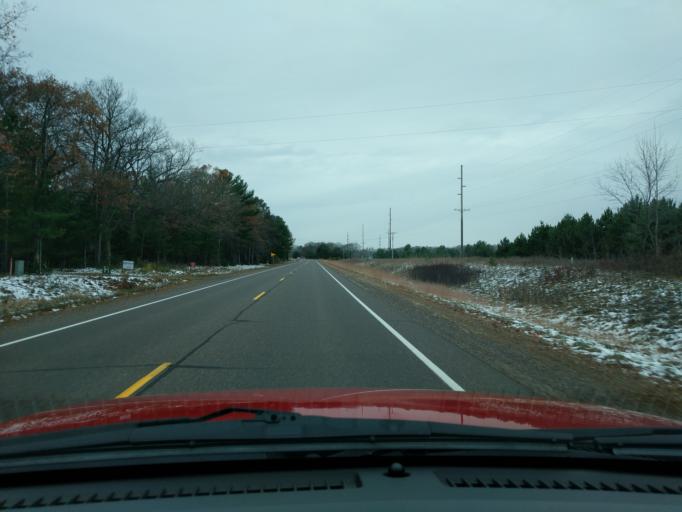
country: US
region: Wisconsin
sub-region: Burnett County
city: Siren
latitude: 45.8218
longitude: -92.2483
